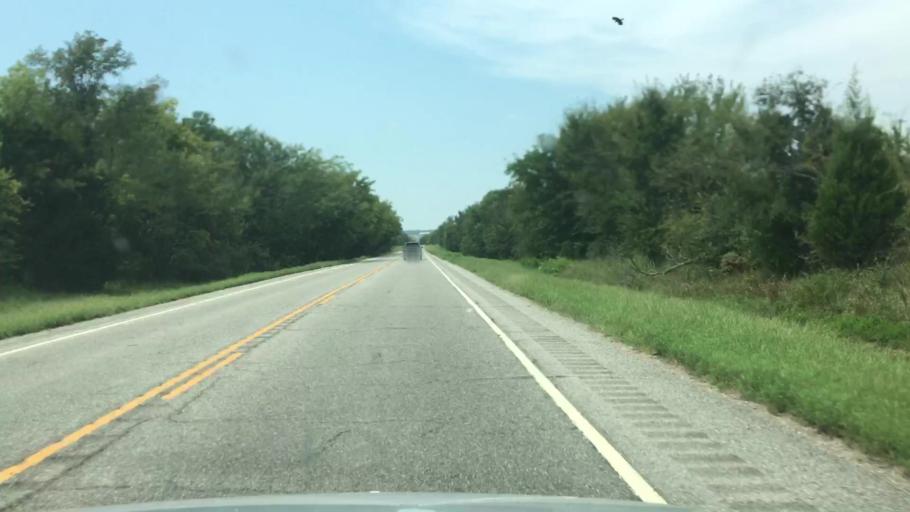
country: US
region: Oklahoma
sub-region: Muskogee County
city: Fort Gibson
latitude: 35.9370
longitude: -95.2001
